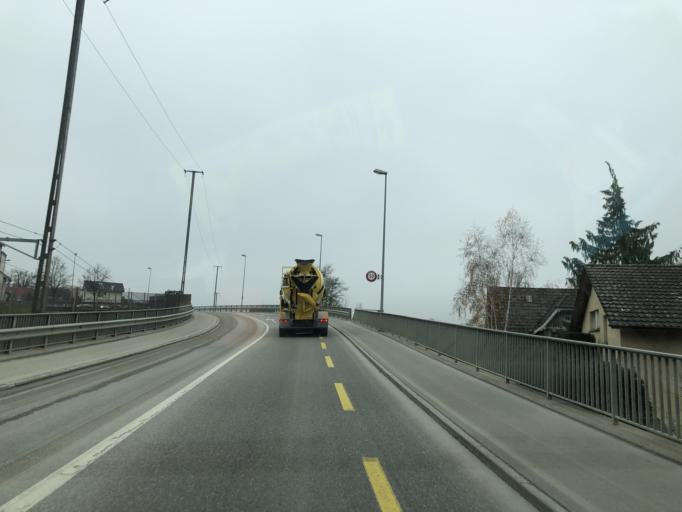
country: CH
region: Aargau
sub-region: Bezirk Baden
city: Gebenstorf
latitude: 47.4927
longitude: 8.2420
